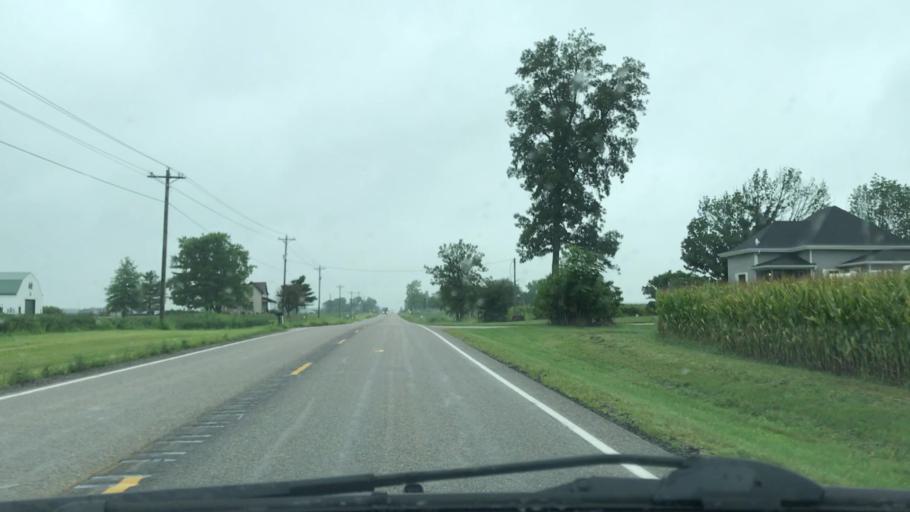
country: US
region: Indiana
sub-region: Boone County
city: Lebanon
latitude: 40.1264
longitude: -86.4504
